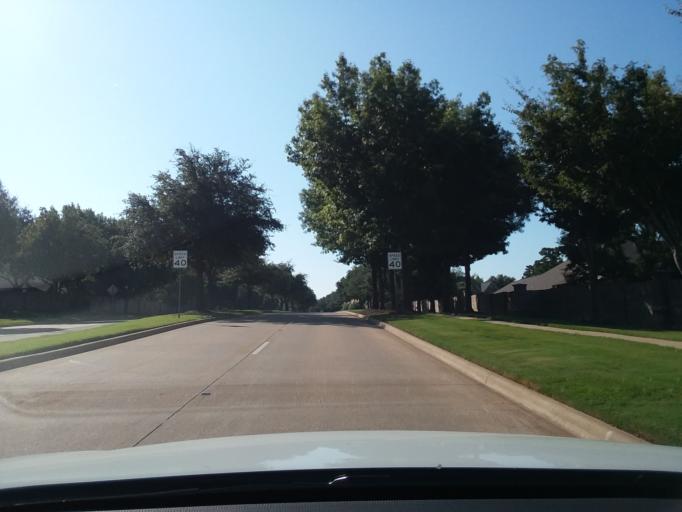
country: US
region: Texas
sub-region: Denton County
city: Flower Mound
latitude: 33.0292
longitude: -97.0962
